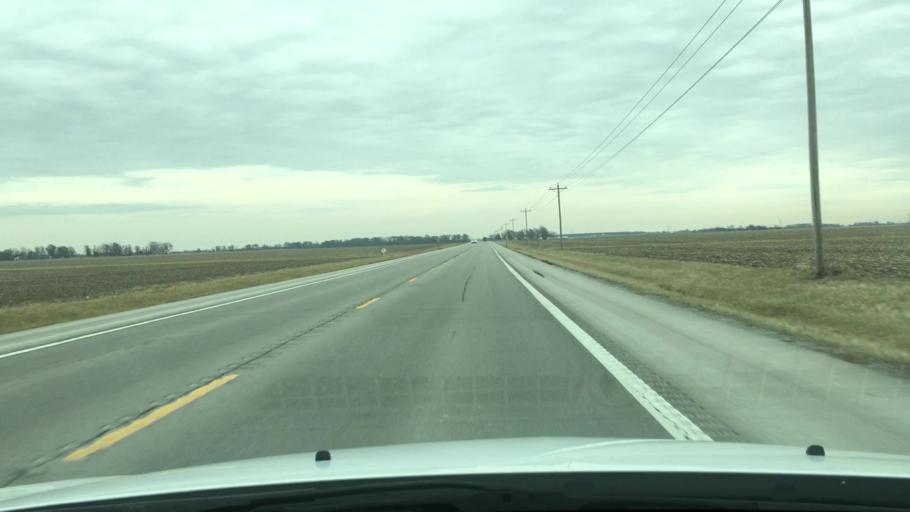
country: US
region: Missouri
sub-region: Audrain County
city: Mexico
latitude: 39.1627
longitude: -91.7693
